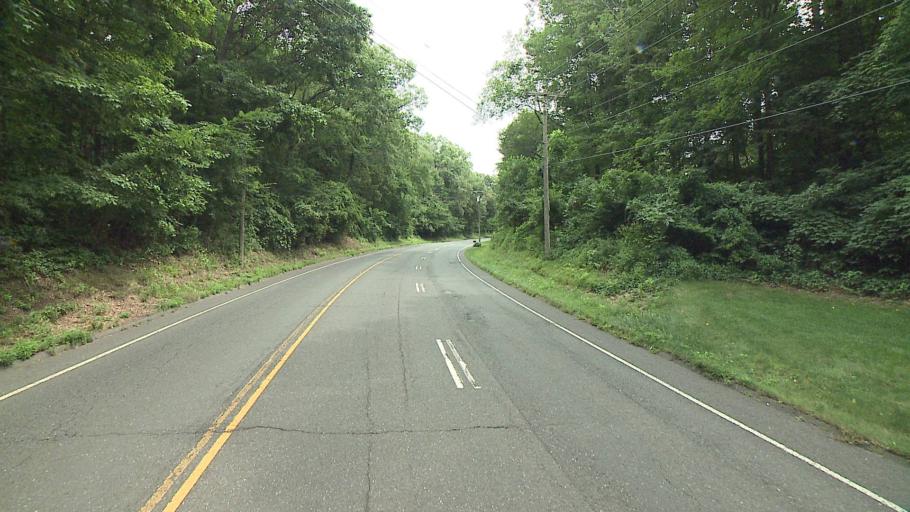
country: US
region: Connecticut
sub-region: Litchfield County
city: Woodbury Center
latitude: 41.5331
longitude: -73.1899
